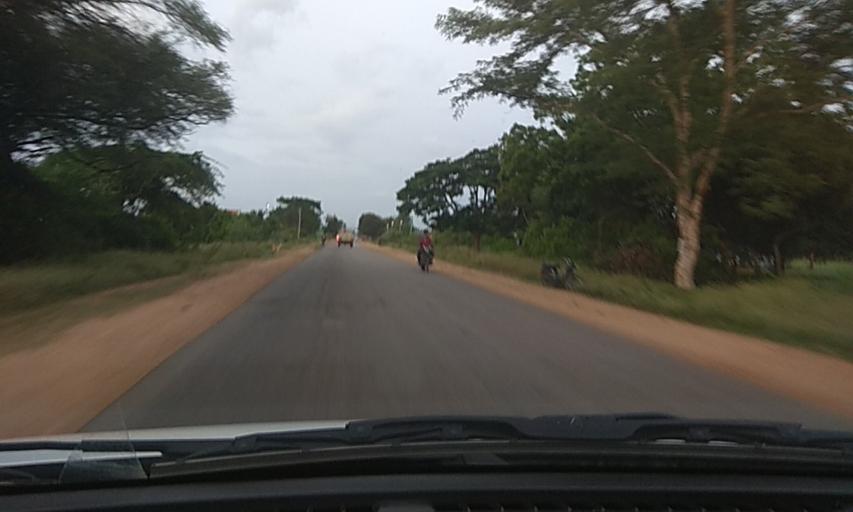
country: IN
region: Karnataka
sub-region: Chamrajnagar
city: Gundlupet
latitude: 11.8110
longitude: 76.7342
